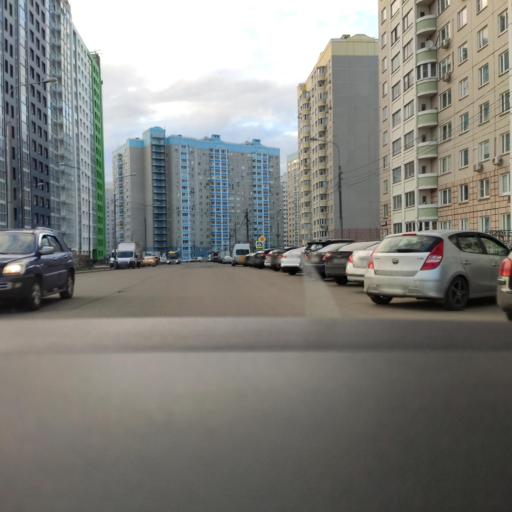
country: RU
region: Moskovskaya
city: Vidnoye
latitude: 55.5386
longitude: 37.7171
